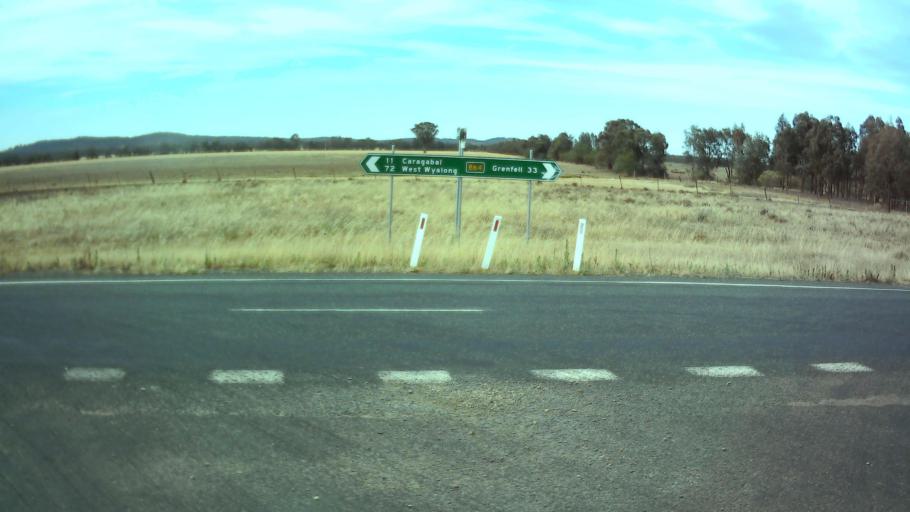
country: AU
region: New South Wales
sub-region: Weddin
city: Grenfell
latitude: -33.8563
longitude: 147.8608
